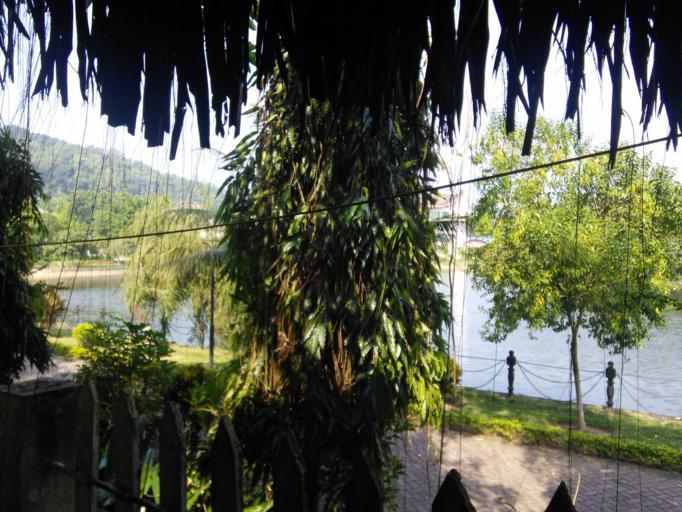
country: VN
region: Lao Cai
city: Lao Cai
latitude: 22.4843
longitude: 103.9684
